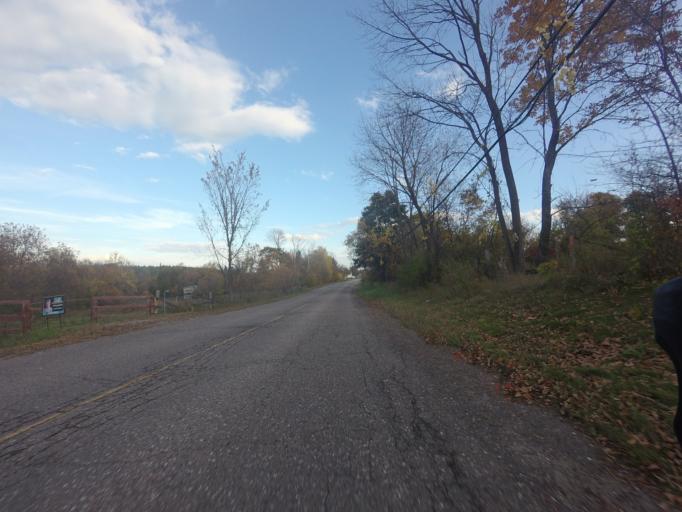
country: CA
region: Ontario
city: Pembroke
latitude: 45.5336
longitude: -77.0934
